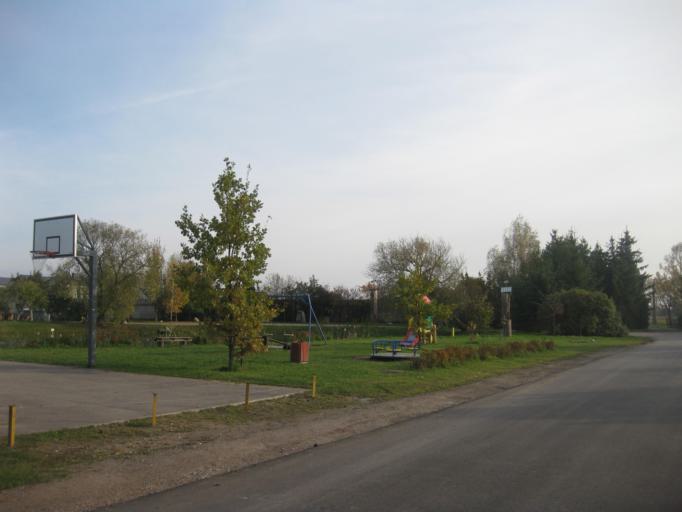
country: LT
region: Kauno apskritis
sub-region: Kaunas
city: Aleksotas
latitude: 54.8896
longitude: 23.8748
